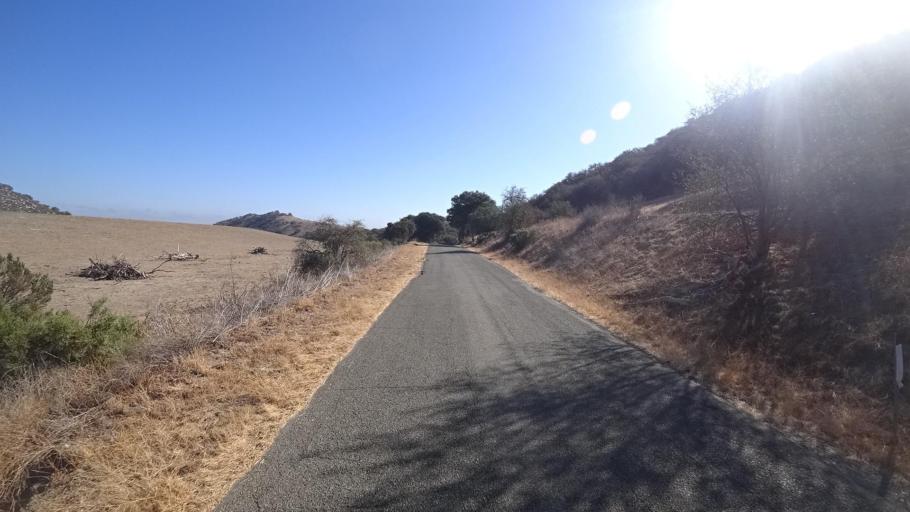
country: US
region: California
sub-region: Monterey County
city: King City
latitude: 36.0604
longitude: -121.0459
